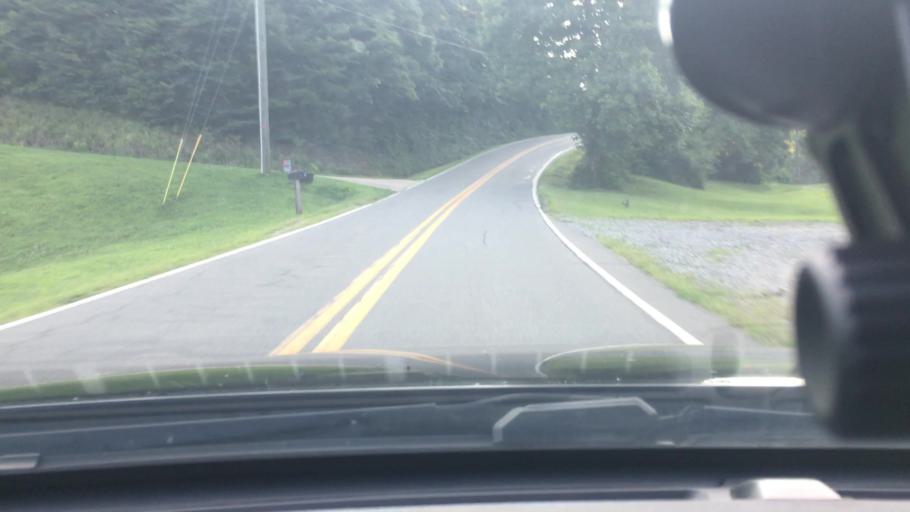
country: US
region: North Carolina
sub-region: McDowell County
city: West Marion
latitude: 35.6281
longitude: -81.9927
